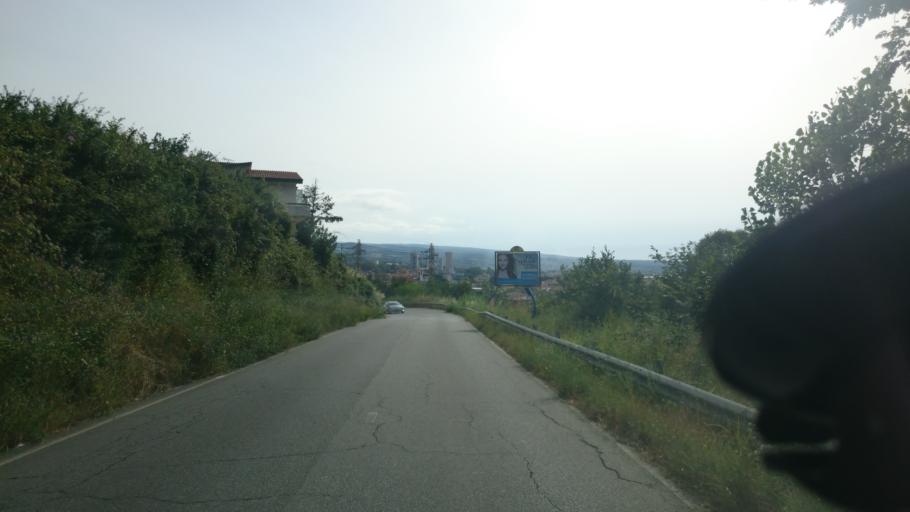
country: IT
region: Calabria
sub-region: Provincia di Vibo-Valentia
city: Sant'Onofrio
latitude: 38.7165
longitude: 16.1332
